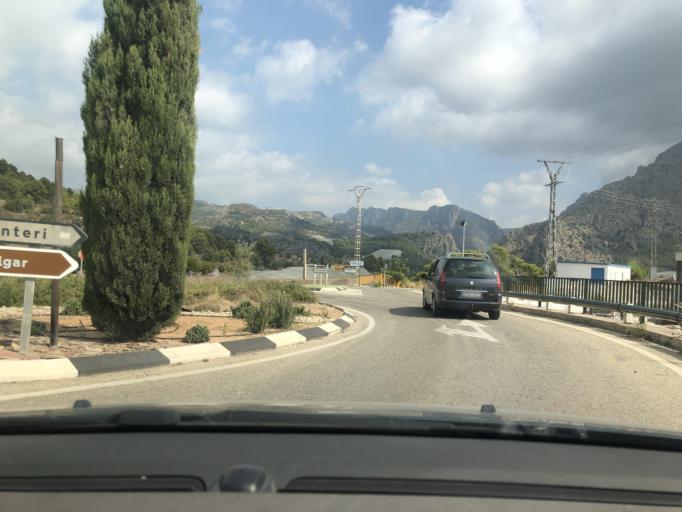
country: ES
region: Valencia
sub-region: Provincia de Alicante
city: Callosa d'En Sarria
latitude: 38.6543
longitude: -0.1070
